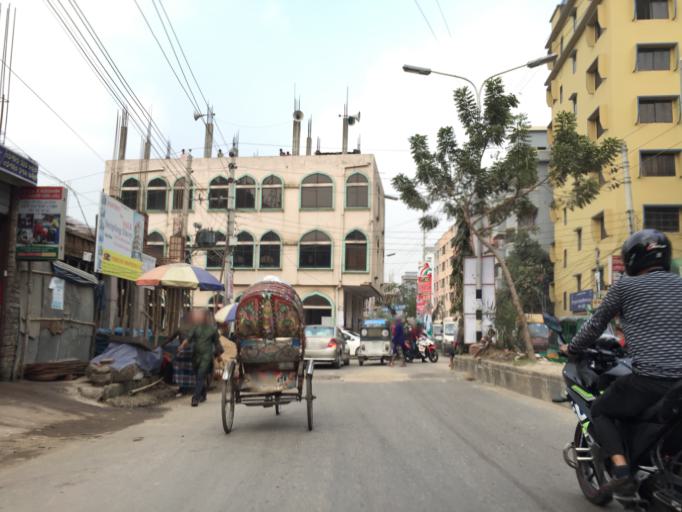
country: BD
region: Dhaka
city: Azimpur
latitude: 23.7823
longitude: 90.3685
